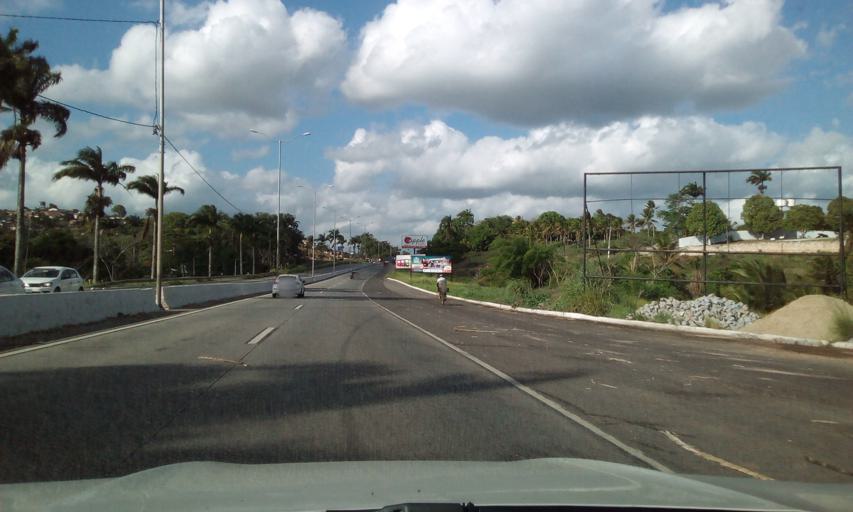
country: BR
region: Pernambuco
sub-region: Palmares
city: Palmares
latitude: -8.6732
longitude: -35.5761
